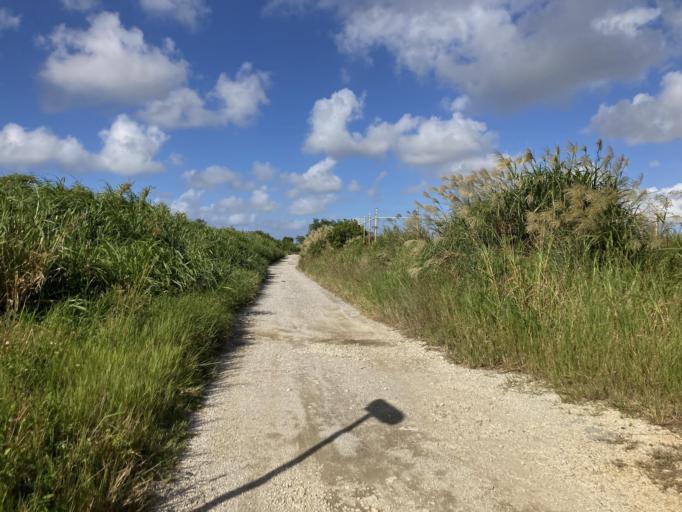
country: JP
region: Okinawa
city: Itoman
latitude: 26.0811
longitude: 127.6648
